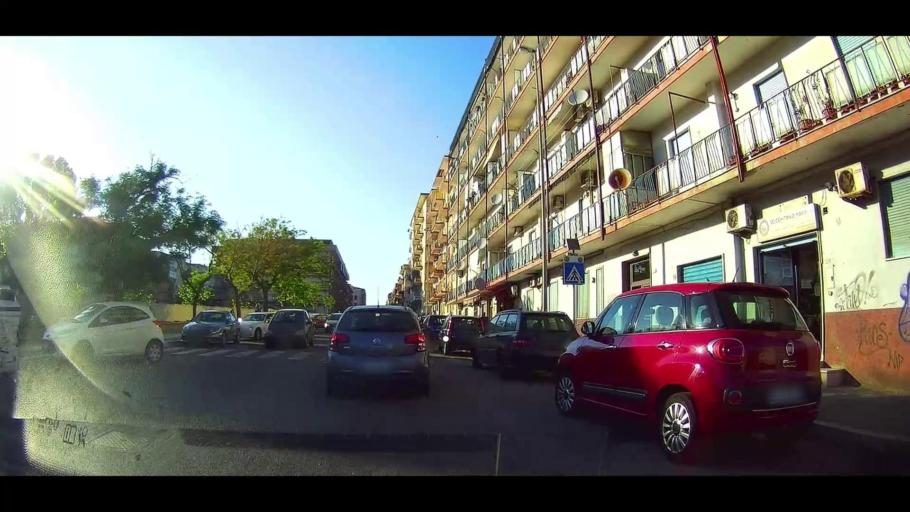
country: IT
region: Calabria
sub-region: Provincia di Crotone
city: Crotone
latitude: 39.0755
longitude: 17.1289
